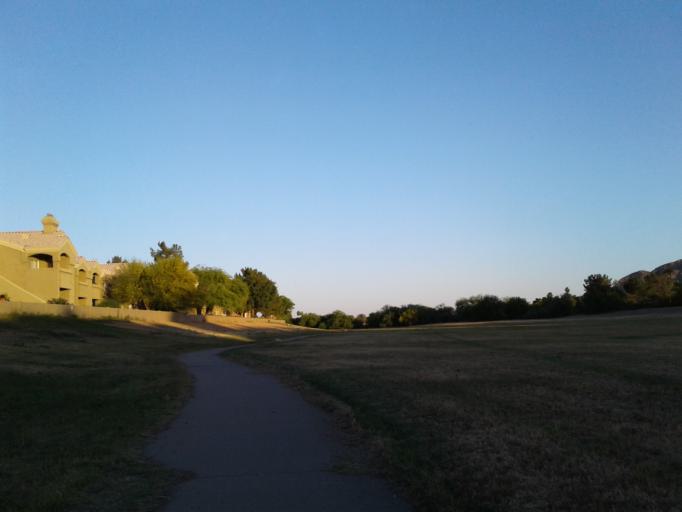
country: US
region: Arizona
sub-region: Maricopa County
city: Paradise Valley
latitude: 33.5809
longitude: -111.9673
